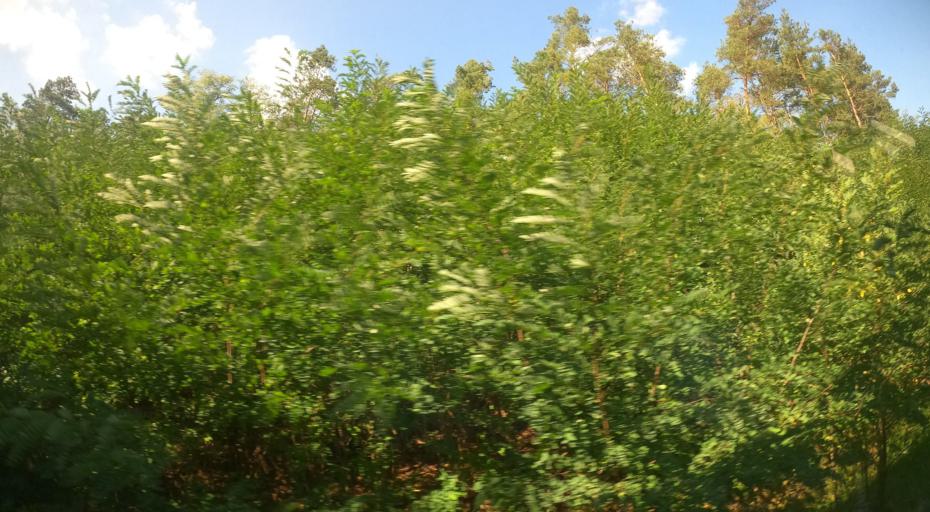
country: PL
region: Lubusz
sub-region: Powiat zielonogorski
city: Swidnica
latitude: 51.9271
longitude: 15.3844
